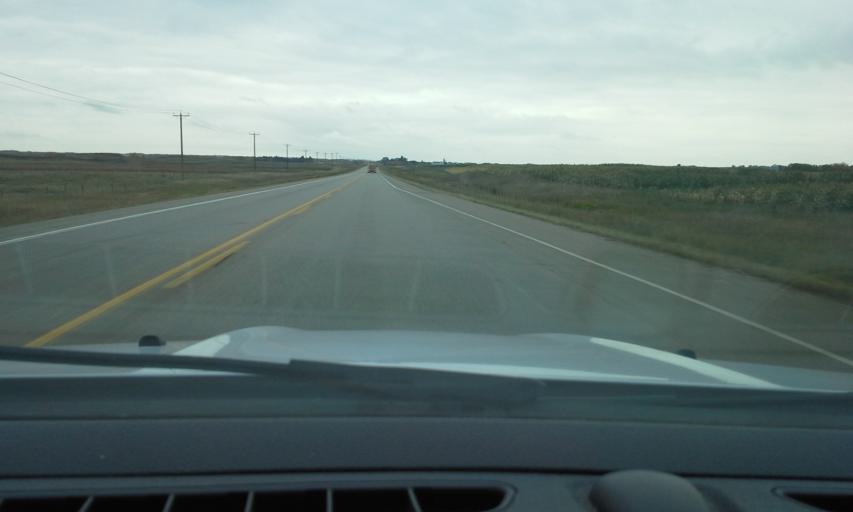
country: CA
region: Saskatchewan
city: Lloydminster
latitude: 53.2779
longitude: -109.8802
